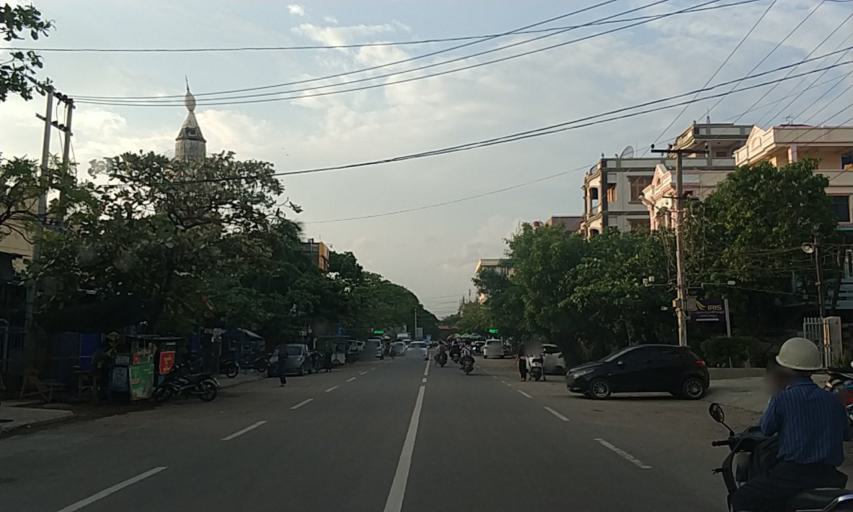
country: MM
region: Mandalay
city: Mandalay
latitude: 21.9754
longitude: 96.0918
